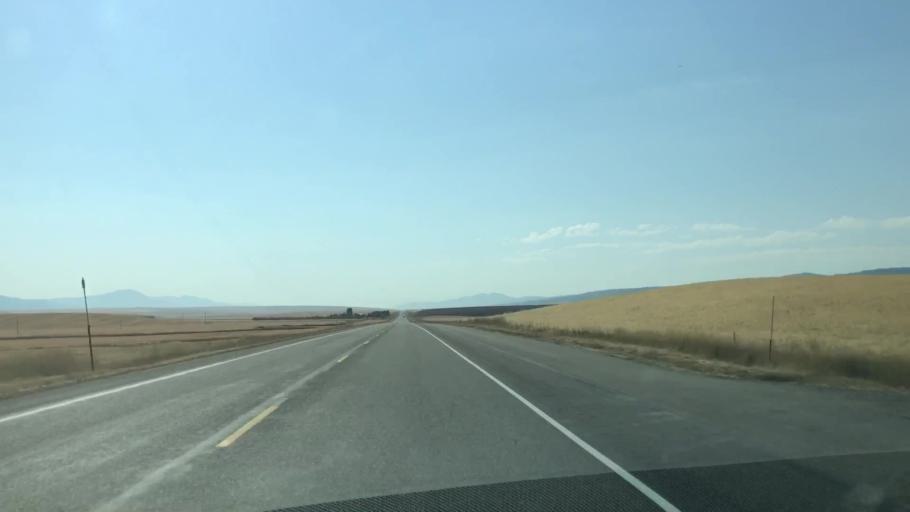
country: US
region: Idaho
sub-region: Madison County
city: Rexburg
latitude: 43.5779
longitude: -111.5659
